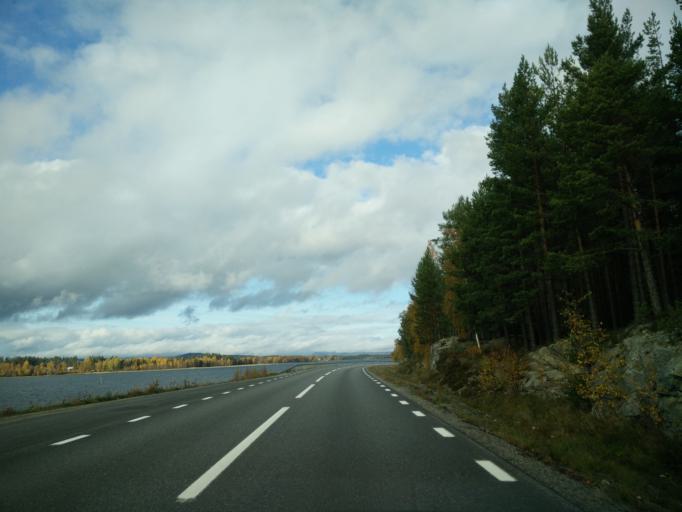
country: SE
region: Jaemtland
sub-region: Braecke Kommun
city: Braecke
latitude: 62.3966
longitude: 15.0325
